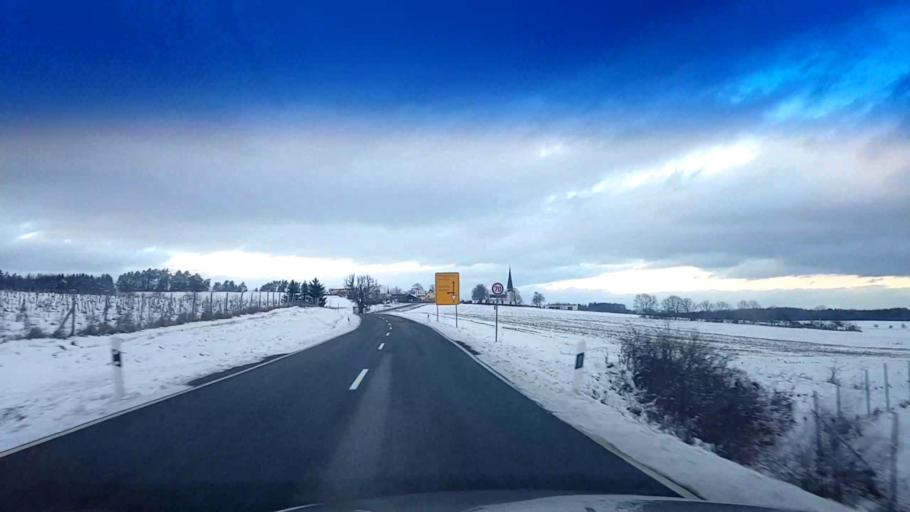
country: DE
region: Bavaria
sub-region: Upper Franconia
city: Poxdorf
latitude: 49.8656
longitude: 11.0893
